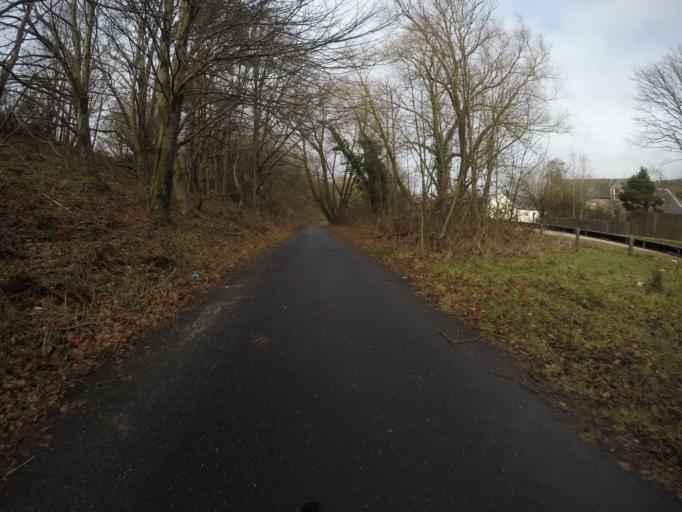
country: GB
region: Scotland
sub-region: North Ayrshire
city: Fairlie
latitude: 55.7371
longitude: -4.8615
